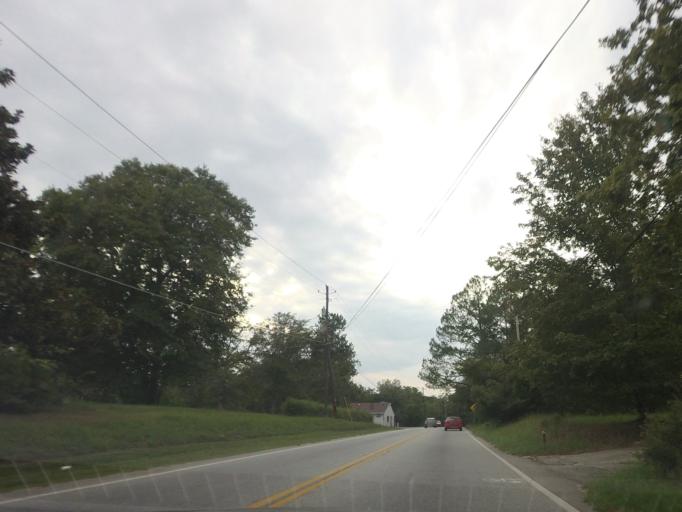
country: US
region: Georgia
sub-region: Bibb County
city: Macon
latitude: 32.8383
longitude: -83.5487
